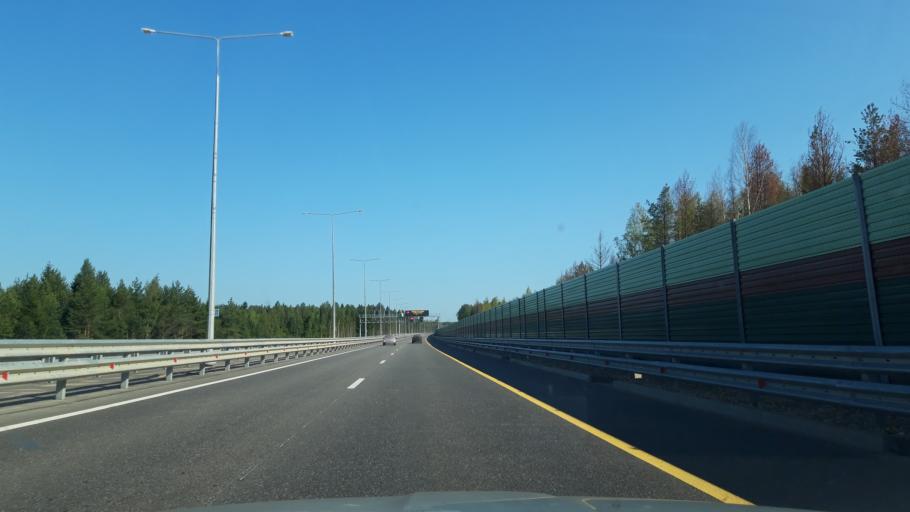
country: RU
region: Moskovskaya
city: Reshetnikovo
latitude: 56.4328
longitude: 36.5456
